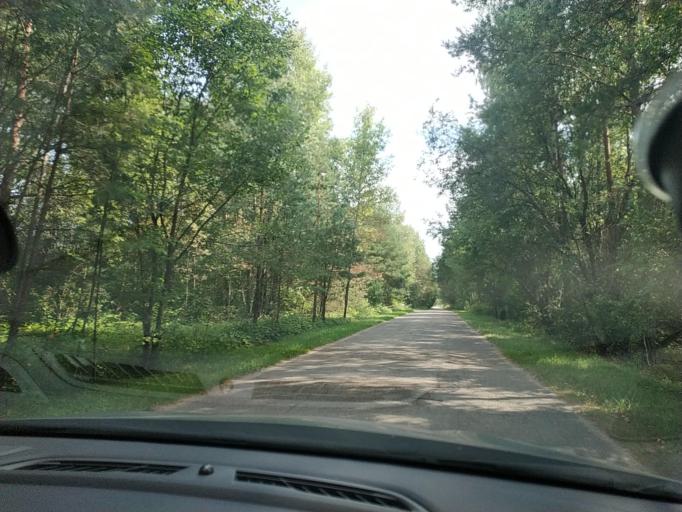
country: LT
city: Nemencine
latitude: 54.8495
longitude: 25.4526
